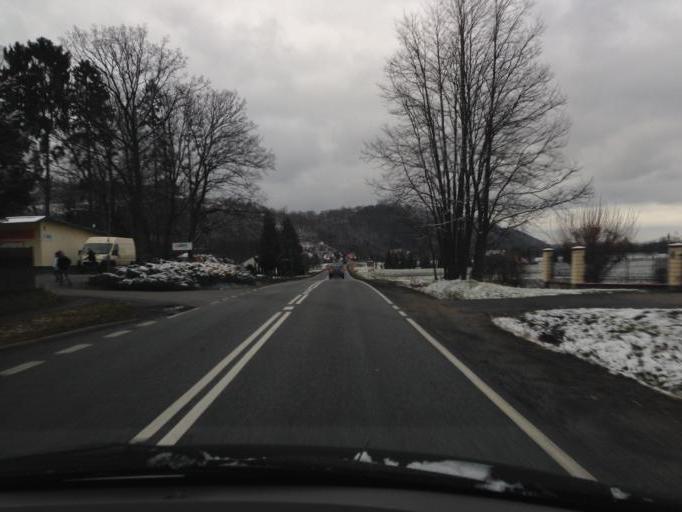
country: PL
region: Lesser Poland Voivodeship
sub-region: Powiat tarnowski
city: Zakliczyn
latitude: 49.8677
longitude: 20.7516
